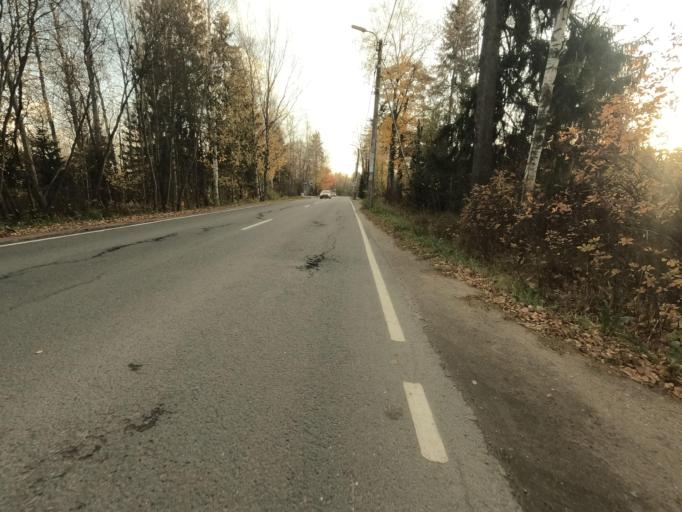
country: RU
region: St.-Petersburg
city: Beloostrov
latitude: 60.1615
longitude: 30.0065
